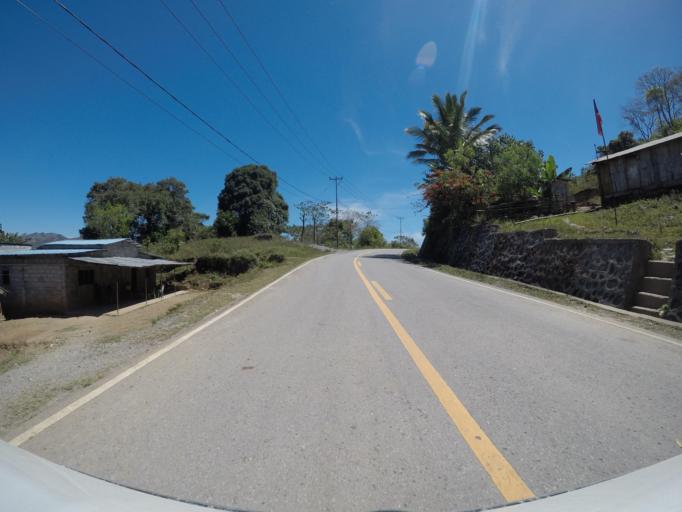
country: TL
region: Manatuto
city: Manatuto
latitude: -8.8000
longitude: 125.9698
